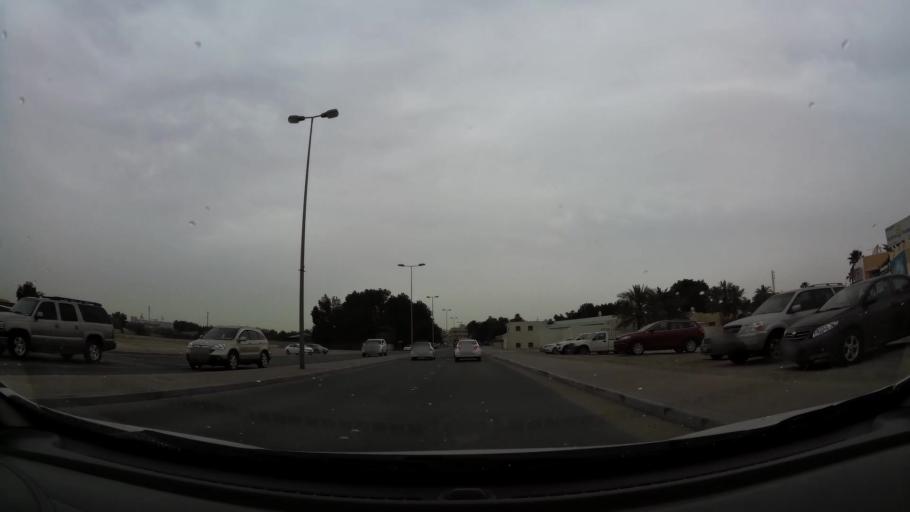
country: BH
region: Manama
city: Jidd Hafs
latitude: 26.2088
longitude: 50.5339
